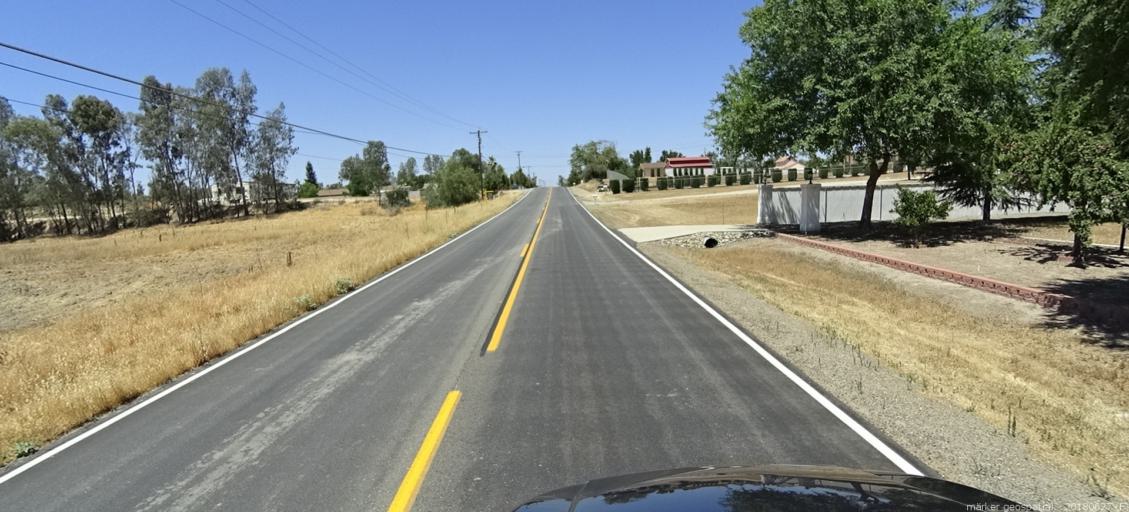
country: US
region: California
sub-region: Madera County
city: Bonadelle Ranchos-Madera Ranchos
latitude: 36.9577
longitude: -119.9119
